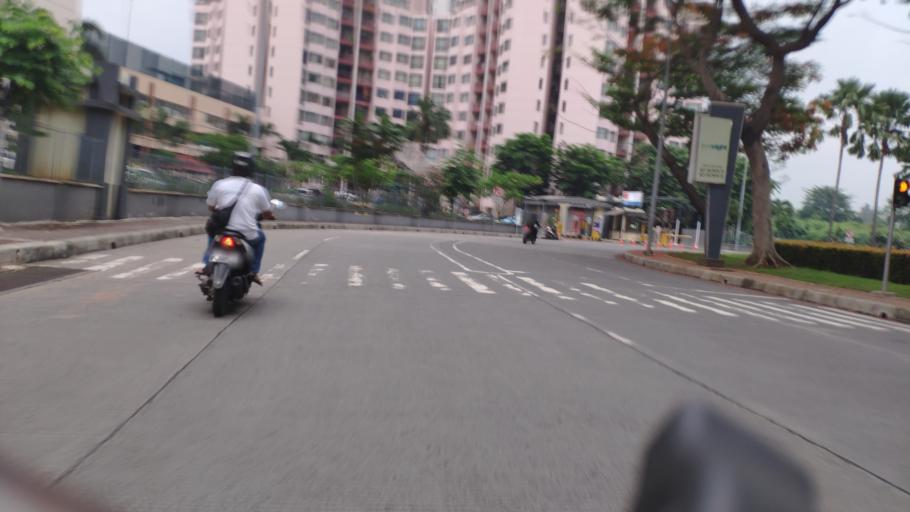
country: ID
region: Jakarta Raya
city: Jakarta
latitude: -6.2178
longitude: 106.8361
